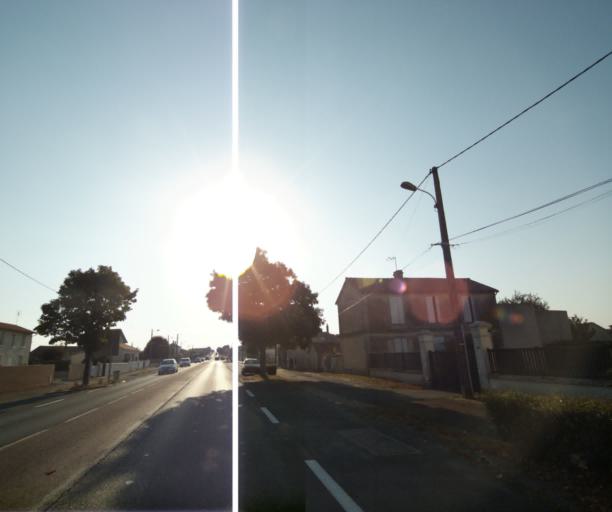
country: FR
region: Poitou-Charentes
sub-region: Departement de la Charente-Maritime
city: Tonnay-Charente
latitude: 45.9501
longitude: -0.9259
